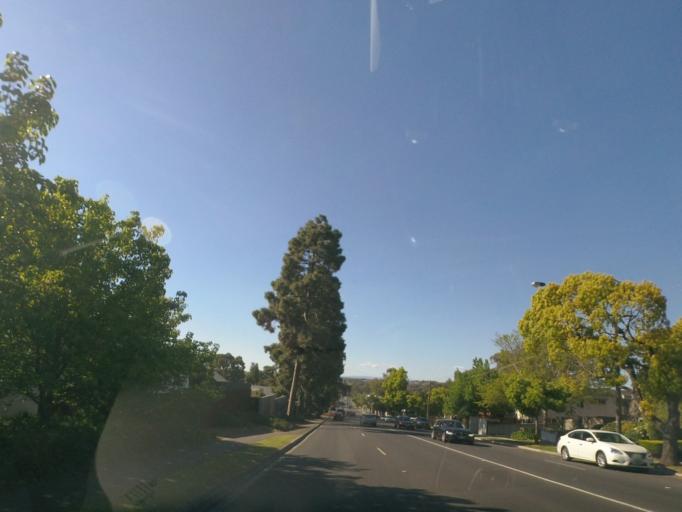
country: AU
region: Victoria
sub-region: Boroondara
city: Kew
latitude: -37.7967
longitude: 145.0306
